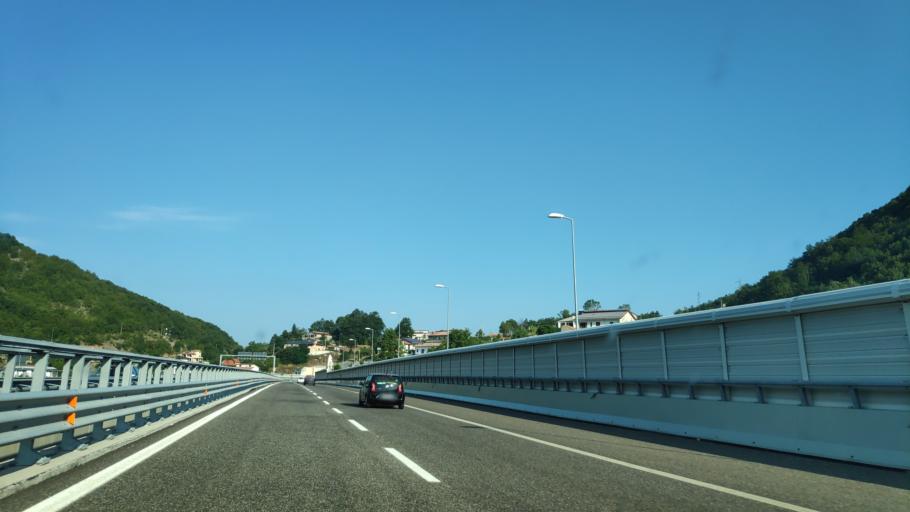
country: IT
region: Basilicate
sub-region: Provincia di Potenza
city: Lauria
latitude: 40.0194
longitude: 15.8848
